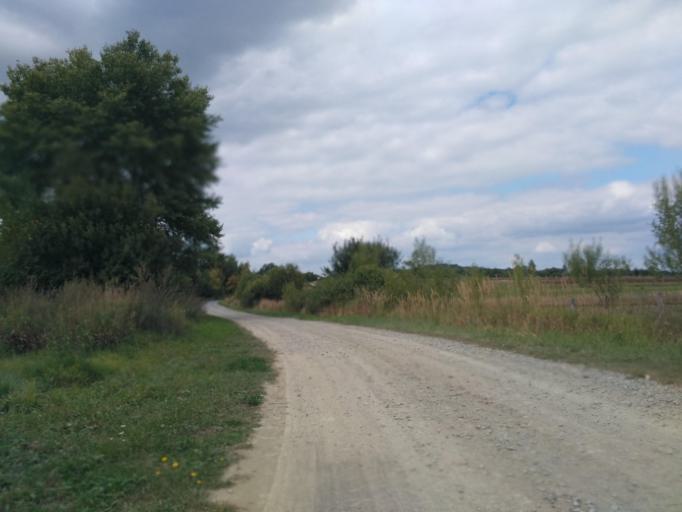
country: PL
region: Subcarpathian Voivodeship
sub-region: Powiat rzeszowski
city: Dynow
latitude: 49.7671
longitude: 22.2895
